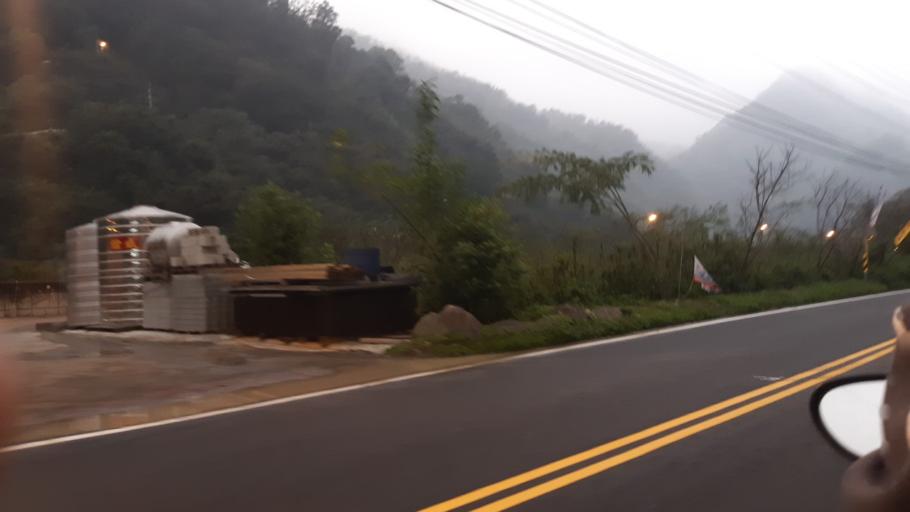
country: TW
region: Taiwan
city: Daxi
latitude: 24.6986
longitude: 121.1939
